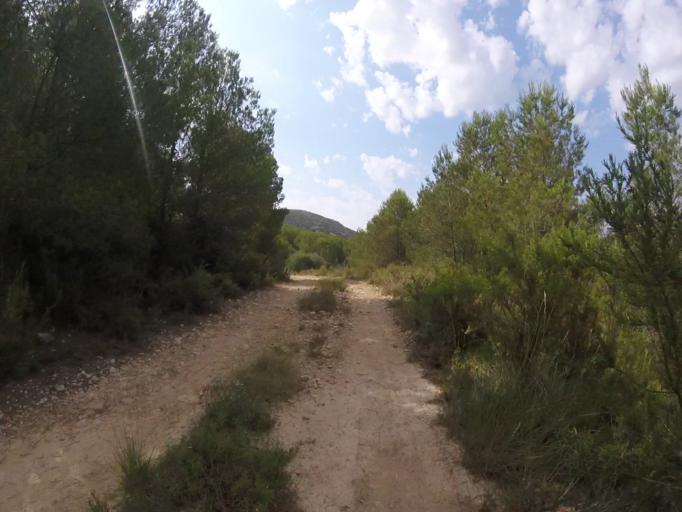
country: ES
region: Valencia
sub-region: Provincia de Castello
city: Alcala de Xivert
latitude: 40.3578
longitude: 0.1987
